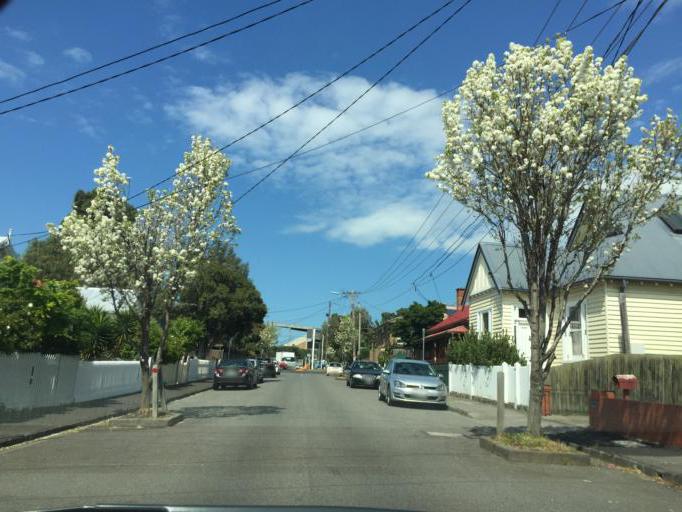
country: AU
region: Victoria
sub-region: Maribyrnong
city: West Footscray
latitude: -37.7974
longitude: 144.8865
